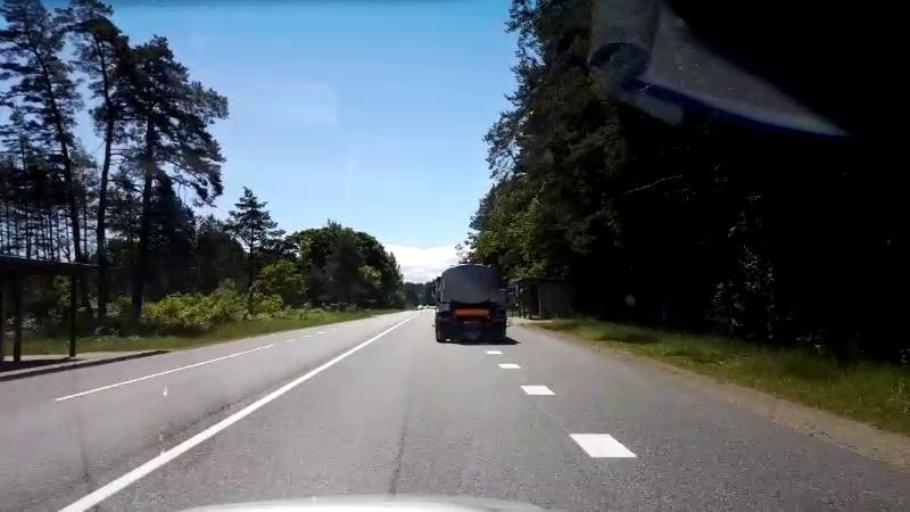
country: LV
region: Saulkrastu
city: Saulkrasti
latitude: 57.3889
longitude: 24.4288
